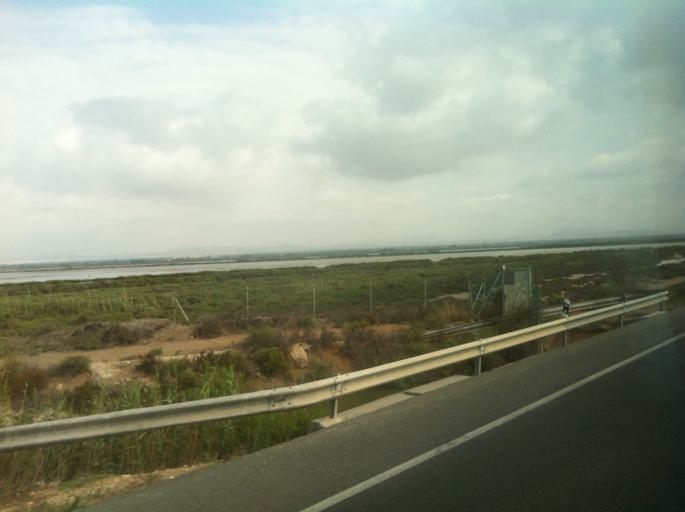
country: ES
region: Valencia
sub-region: Provincia de Alicante
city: Santa Pola
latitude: 38.1784
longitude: -0.6197
